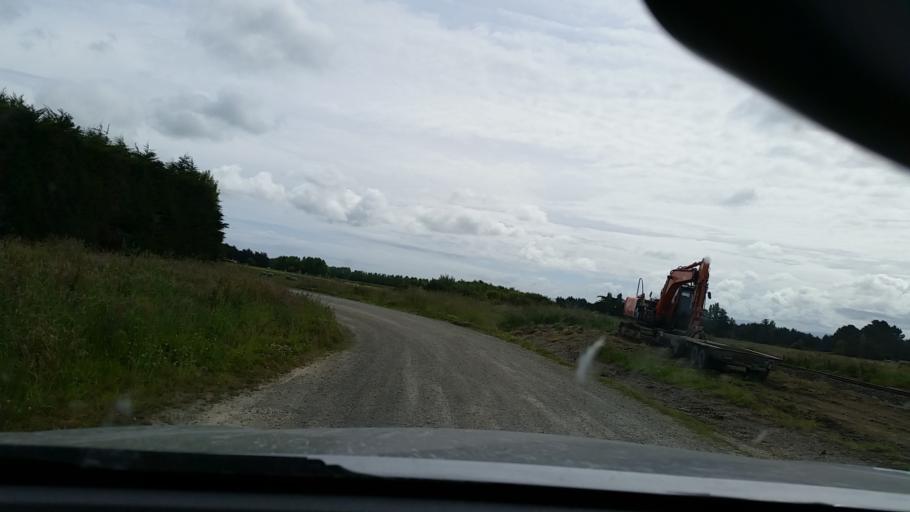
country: NZ
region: Southland
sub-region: Invercargill City
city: Invercargill
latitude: -46.2951
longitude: 168.2461
